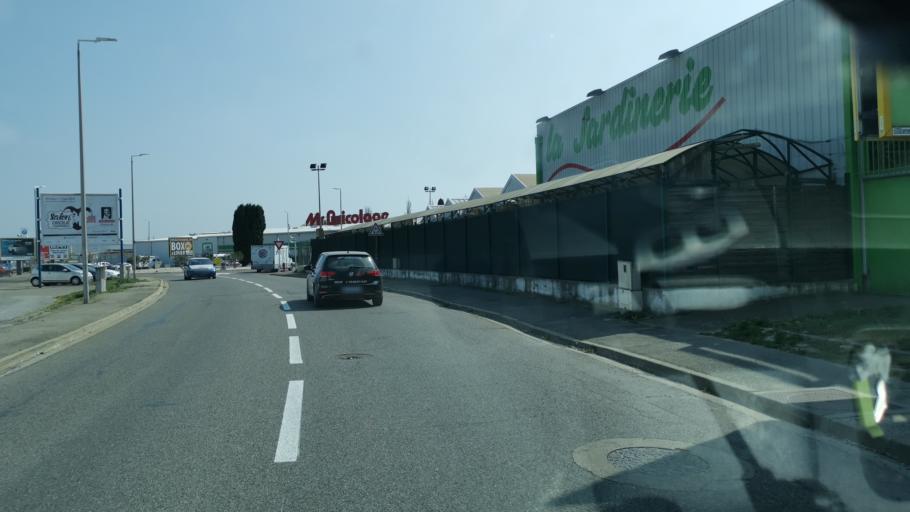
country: FR
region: Provence-Alpes-Cote d'Azur
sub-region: Departement des Bouches-du-Rhone
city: Arles
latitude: 43.6638
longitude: 4.6379
